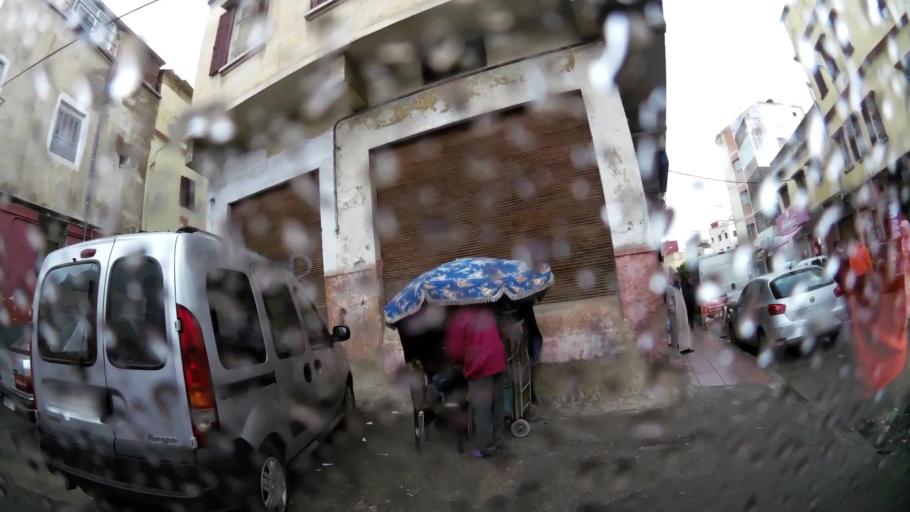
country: MA
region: Grand Casablanca
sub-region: Casablanca
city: Casablanca
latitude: 33.5705
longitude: -7.6043
